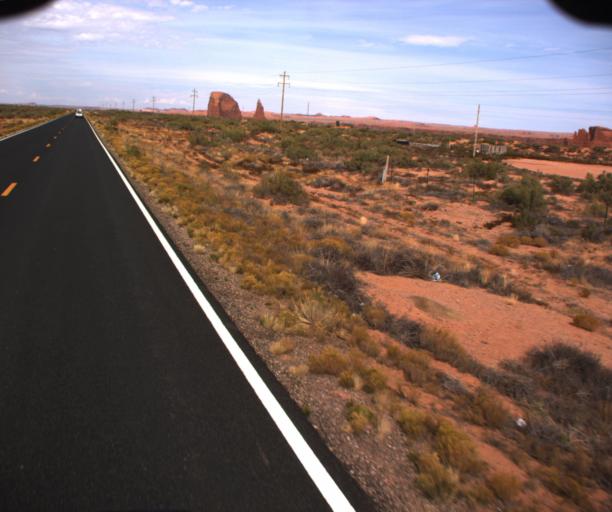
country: US
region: Arizona
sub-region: Apache County
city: Many Farms
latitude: 36.6304
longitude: -109.5849
